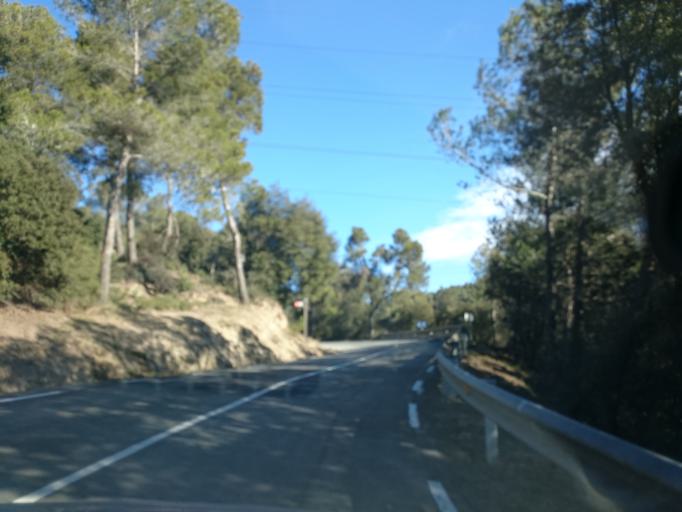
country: ES
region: Catalonia
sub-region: Provincia de Barcelona
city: Molins de Rei
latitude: 41.4276
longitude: 2.0470
